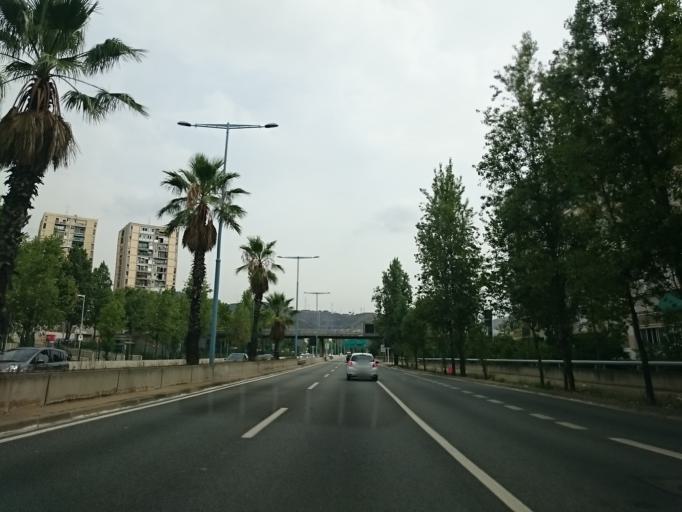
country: ES
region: Catalonia
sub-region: Provincia de Barcelona
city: Horta-Guinardo
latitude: 41.4313
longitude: 2.1456
